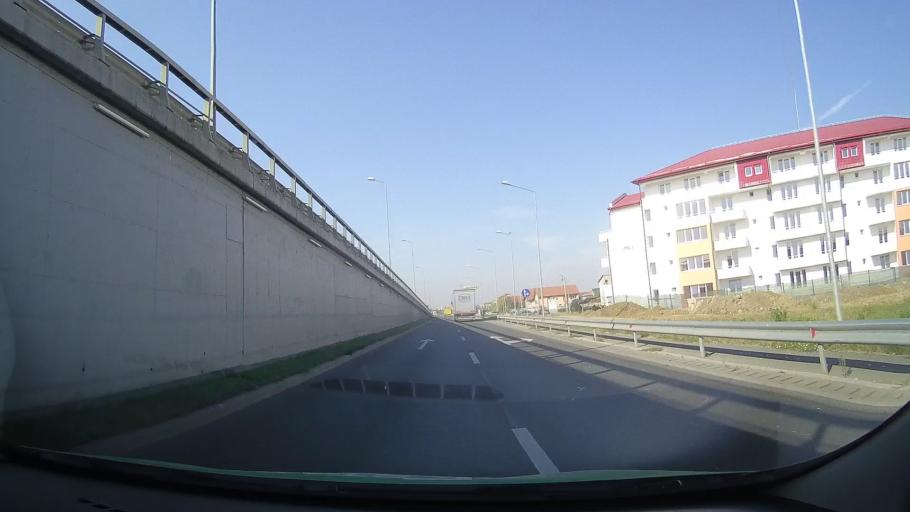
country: RO
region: Bihor
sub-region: Comuna Biharea
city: Oradea
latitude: 47.0465
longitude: 21.9020
